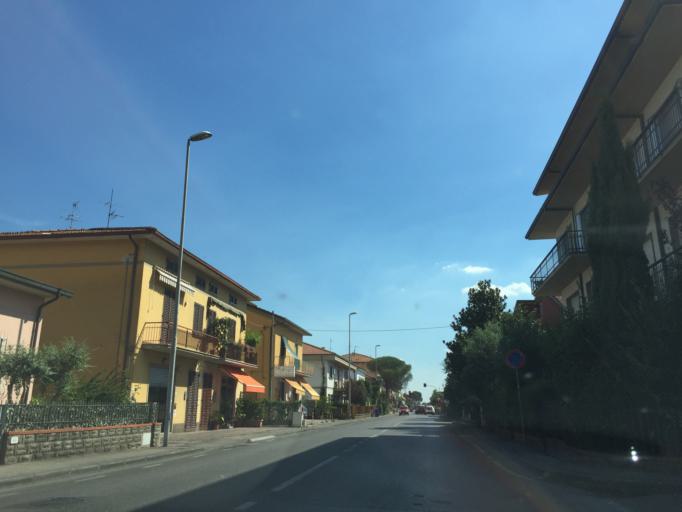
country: IT
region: Tuscany
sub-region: Provincia di Pistoia
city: Monsummano Terme
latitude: 43.8733
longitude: 10.8110
